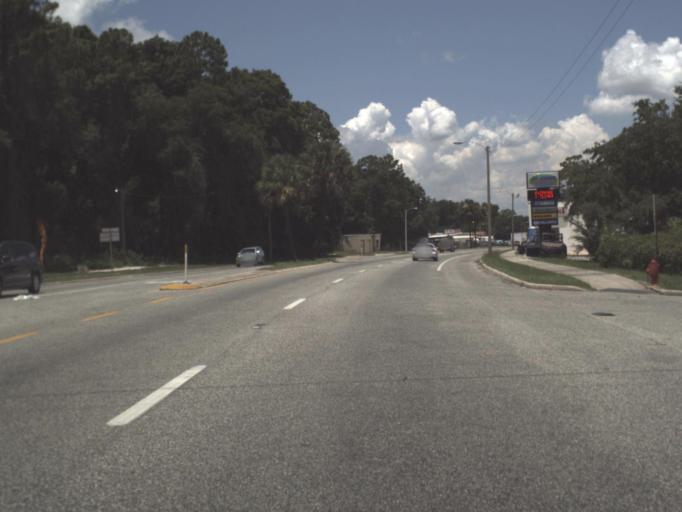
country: US
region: Florida
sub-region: Putnam County
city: Palatka
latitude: 29.6507
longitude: -81.6508
